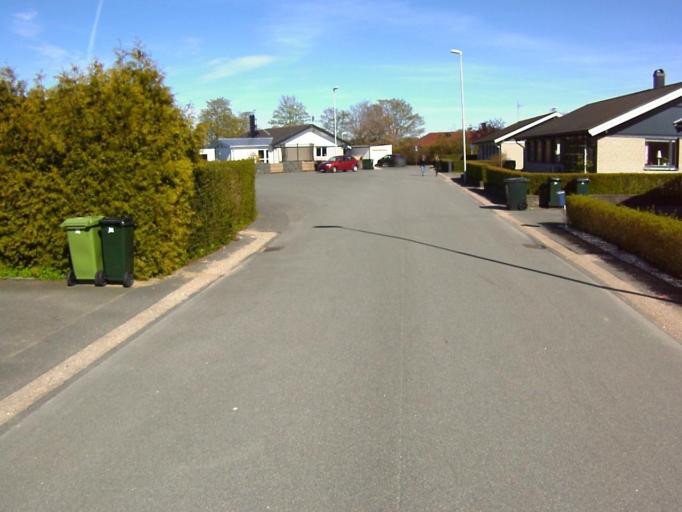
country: SE
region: Skane
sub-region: Kristianstads Kommun
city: Kristianstad
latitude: 56.0097
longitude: 14.1441
